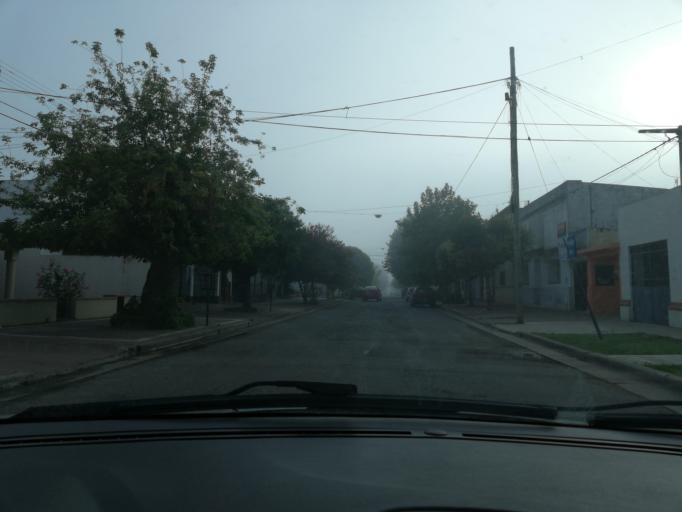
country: AR
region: Buenos Aires
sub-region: Partido de Balcarce
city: Balcarce
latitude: -37.8525
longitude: -58.2609
